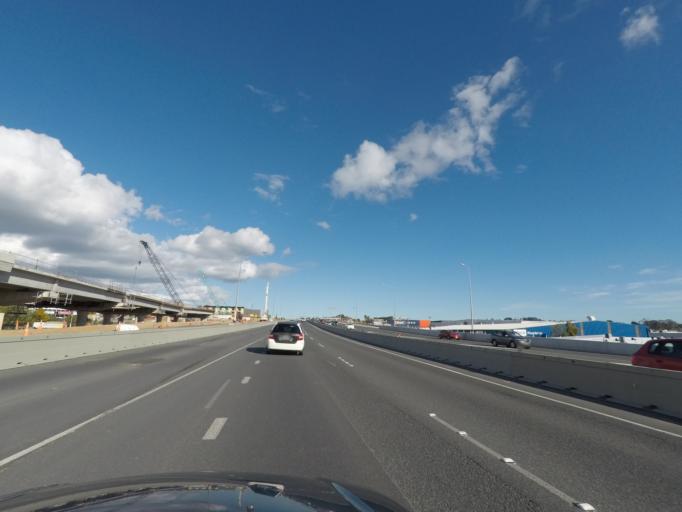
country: NZ
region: Auckland
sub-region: Auckland
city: Rothesay Bay
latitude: -36.7381
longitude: 174.7192
